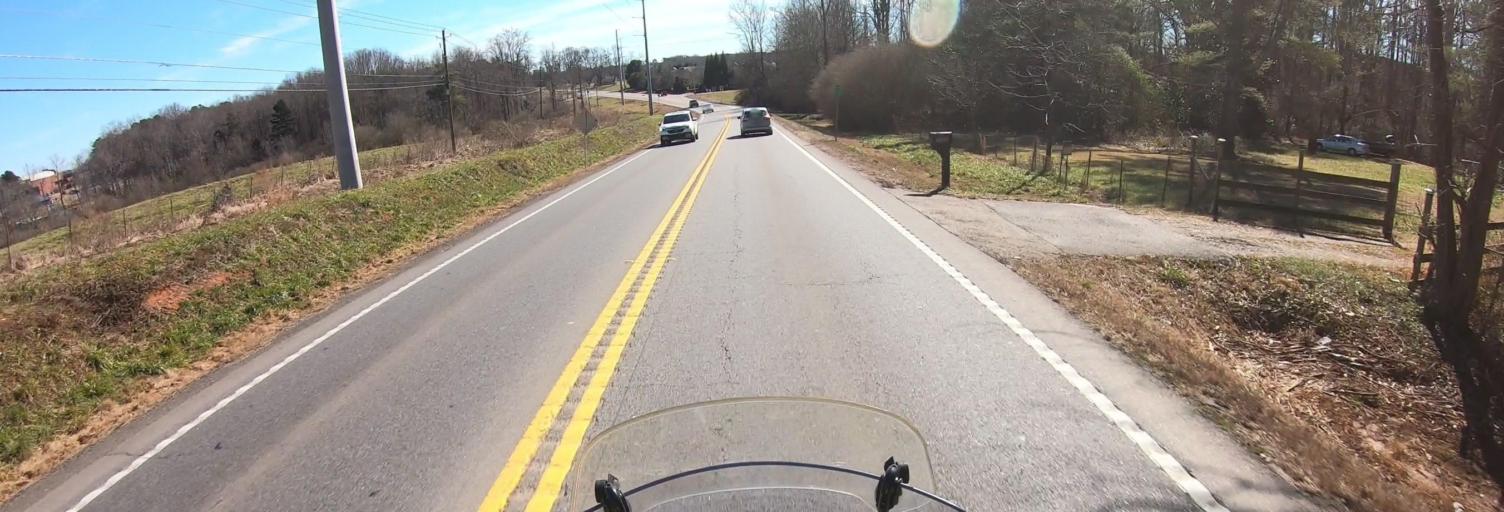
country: US
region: Georgia
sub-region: Forsyth County
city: Cumming
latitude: 34.2774
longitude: -84.1169
